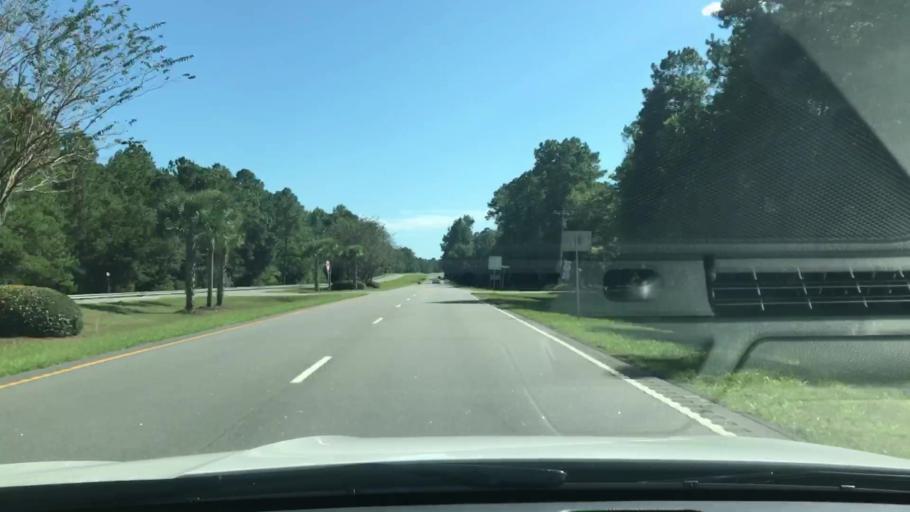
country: US
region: South Carolina
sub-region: Georgetown County
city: Georgetown
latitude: 33.2181
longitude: -79.3799
